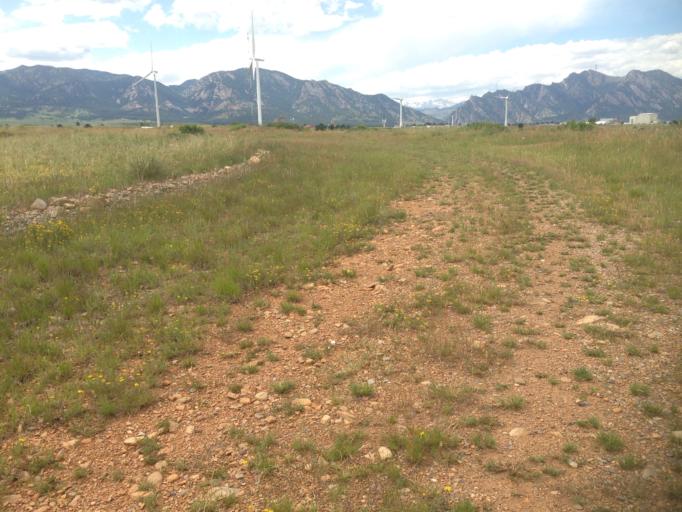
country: US
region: Colorado
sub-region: Boulder County
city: Superior
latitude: 39.9050
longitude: -105.2139
